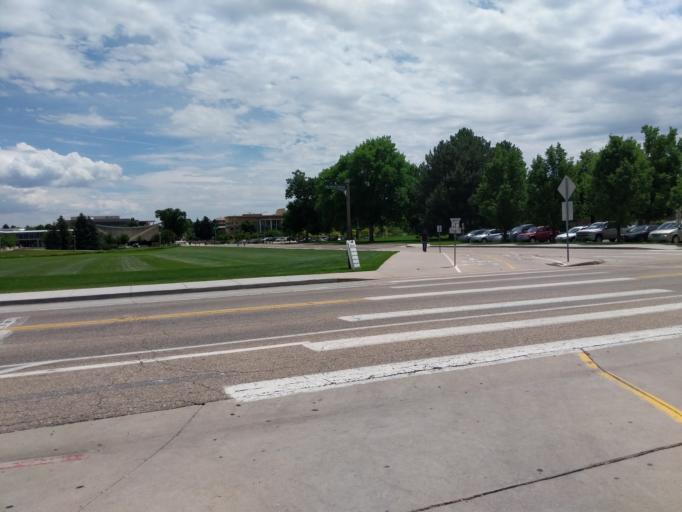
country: US
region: Colorado
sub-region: Larimer County
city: Fort Collins
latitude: 40.5740
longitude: -105.0887
